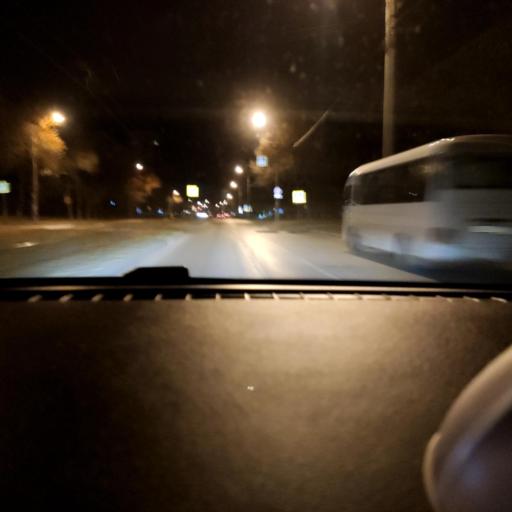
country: RU
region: Samara
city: Samara
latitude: 53.2400
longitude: 50.2141
